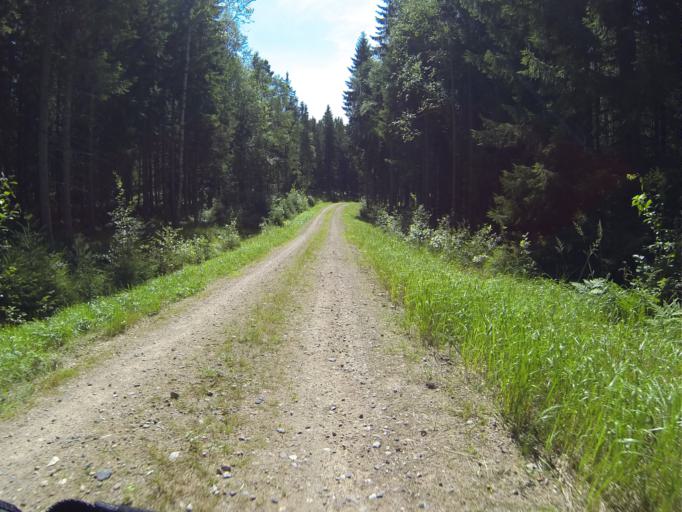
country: FI
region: Varsinais-Suomi
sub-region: Salo
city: Pernioe
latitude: 60.2807
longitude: 23.0601
